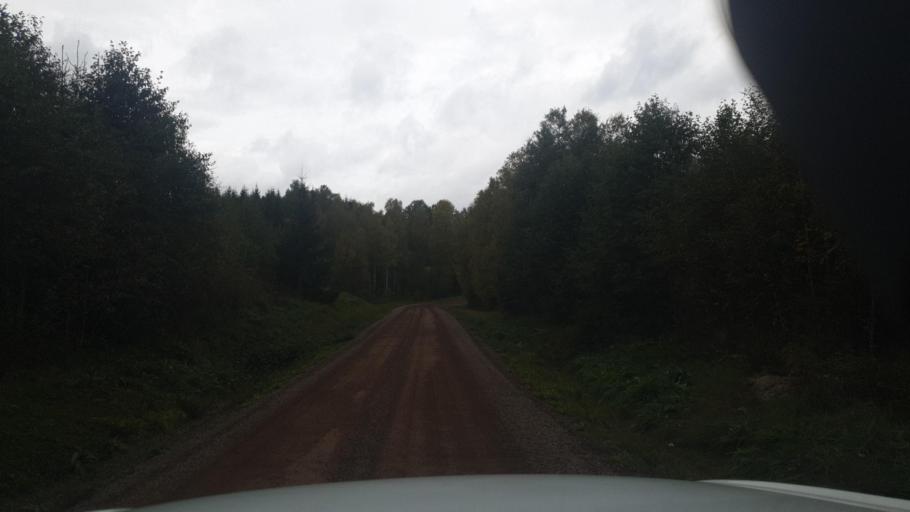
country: SE
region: Vaermland
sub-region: Arvika Kommun
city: Arvika
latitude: 59.9966
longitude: 12.6597
